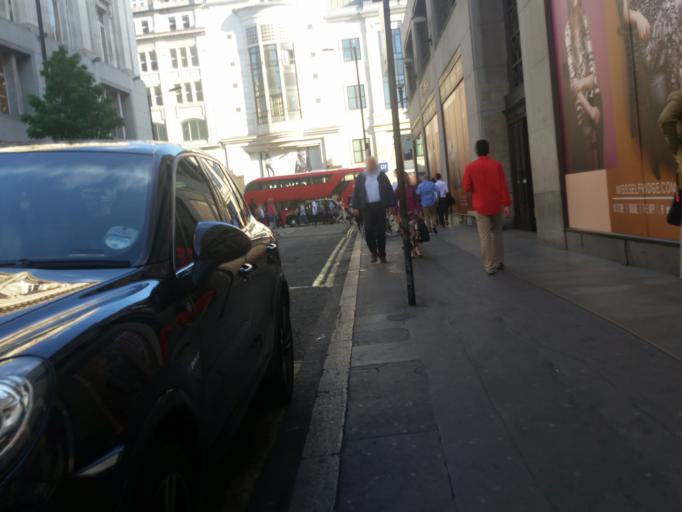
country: GB
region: England
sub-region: Greater London
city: London
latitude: 51.5159
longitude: -0.1410
